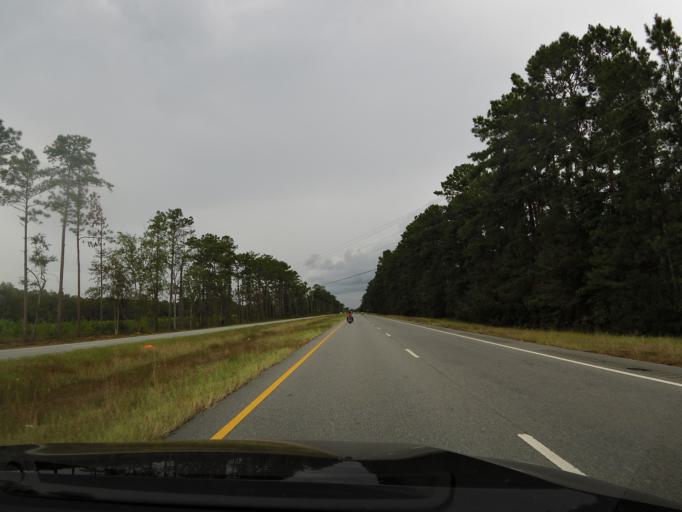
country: US
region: Georgia
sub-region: McIntosh County
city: Darien
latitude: 31.3542
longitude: -81.6124
